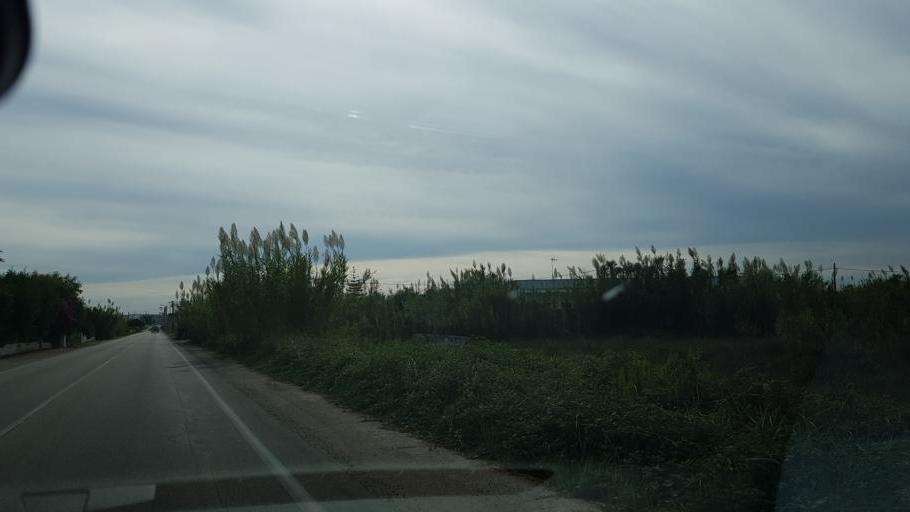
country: IT
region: Apulia
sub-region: Provincia di Lecce
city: Borgagne
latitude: 40.2957
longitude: 18.4154
